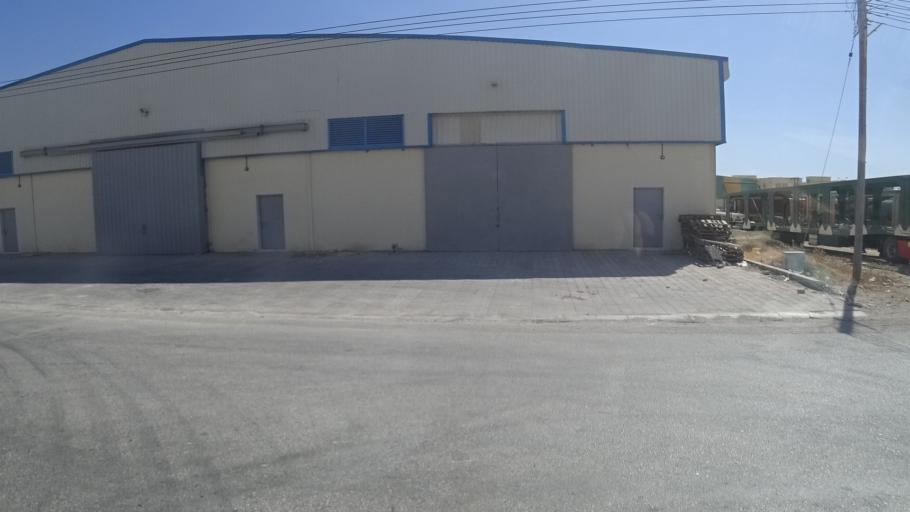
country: OM
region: Zufar
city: Salalah
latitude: 17.0309
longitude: 54.0512
